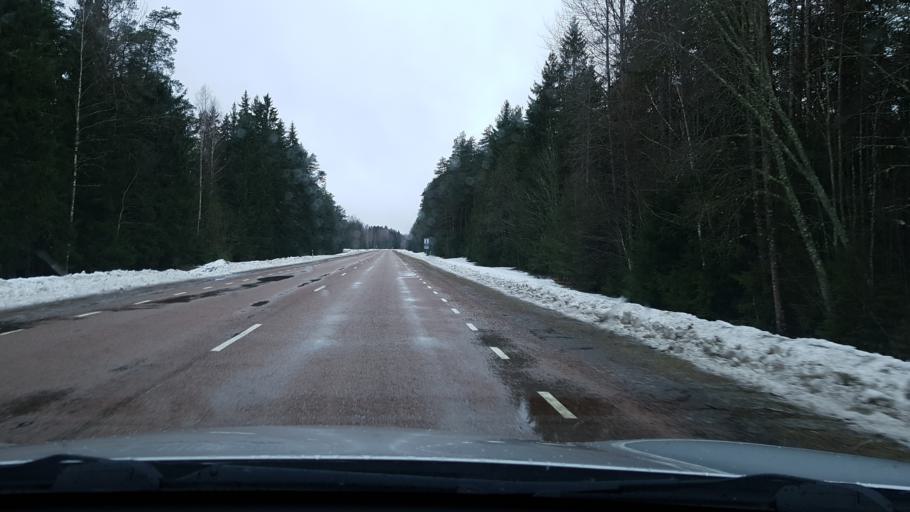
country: EE
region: Vorumaa
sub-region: Voru linn
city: Voru
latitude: 57.7575
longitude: 26.8377
